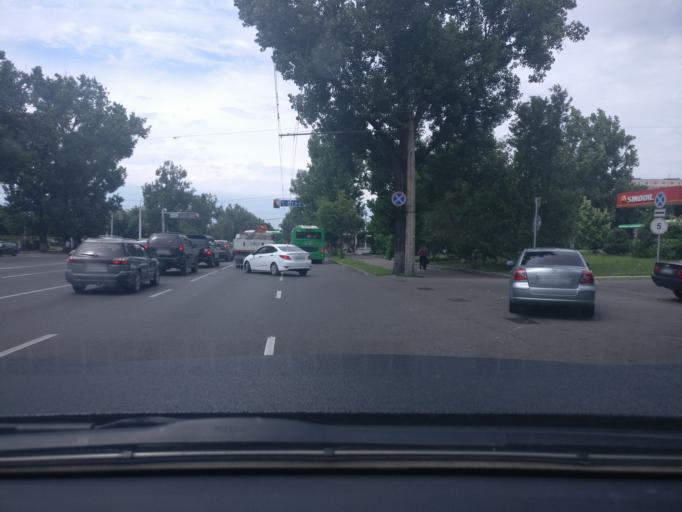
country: KZ
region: Almaty Qalasy
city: Almaty
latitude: 43.2448
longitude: 76.8566
